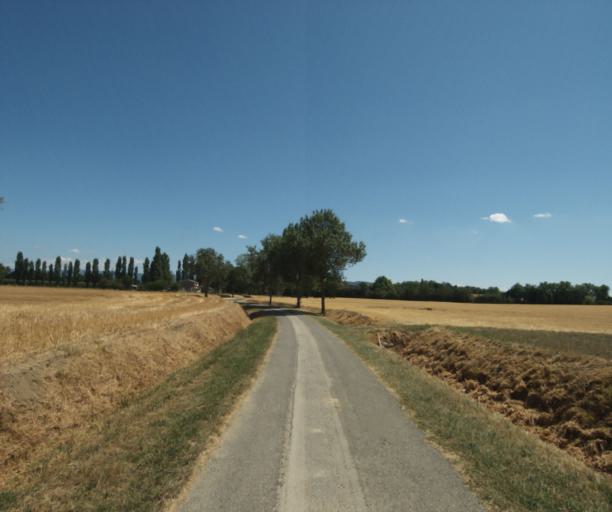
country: FR
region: Midi-Pyrenees
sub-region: Departement de la Haute-Garonne
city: Revel
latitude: 43.4756
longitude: 1.9494
